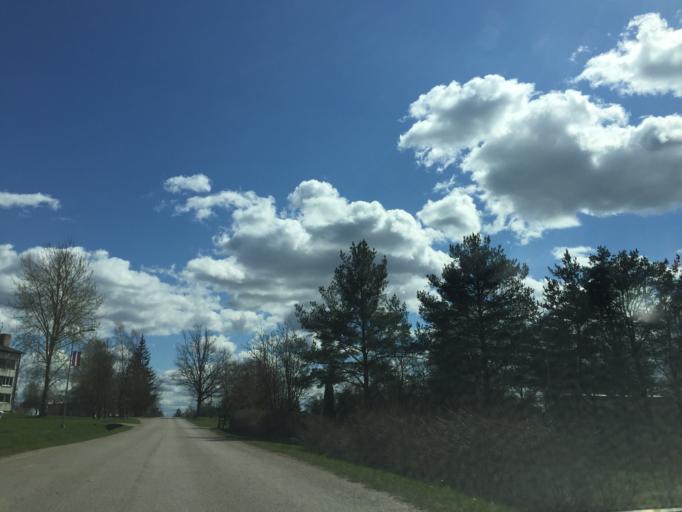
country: LV
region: Rezekne
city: Rezekne
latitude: 56.5655
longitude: 27.1406
